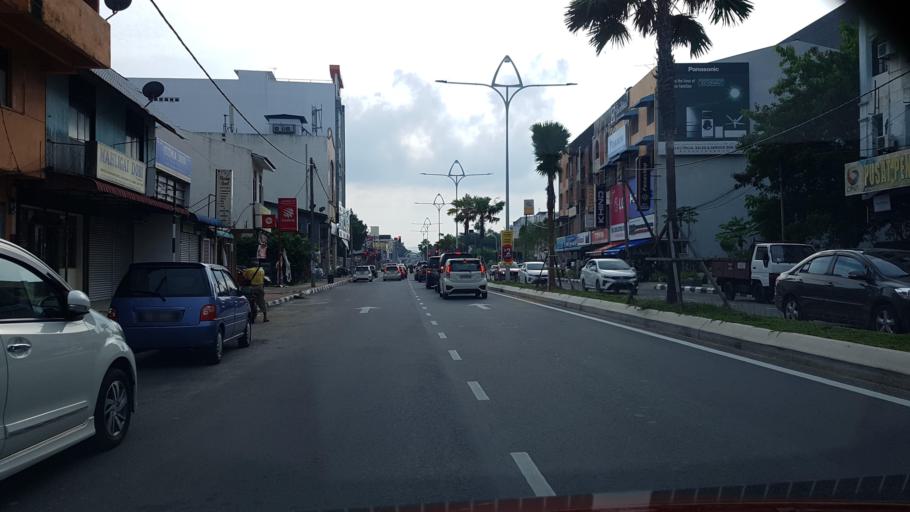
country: MY
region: Terengganu
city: Kuala Terengganu
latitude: 5.3364
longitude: 103.1430
